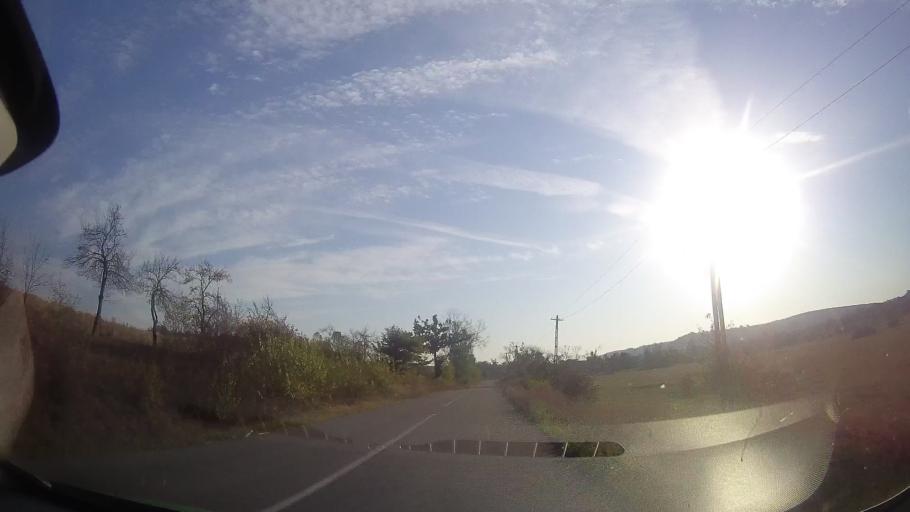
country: RO
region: Timis
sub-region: Comuna Masloc
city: Masloc
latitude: 45.9803
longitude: 21.5095
